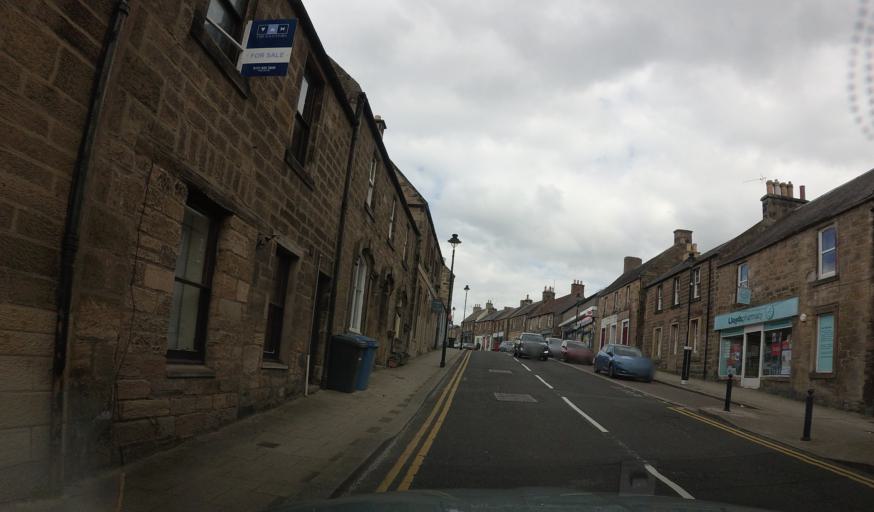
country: GB
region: Scotland
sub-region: Midlothian
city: Gorebridge
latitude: 55.8412
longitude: -3.0480
